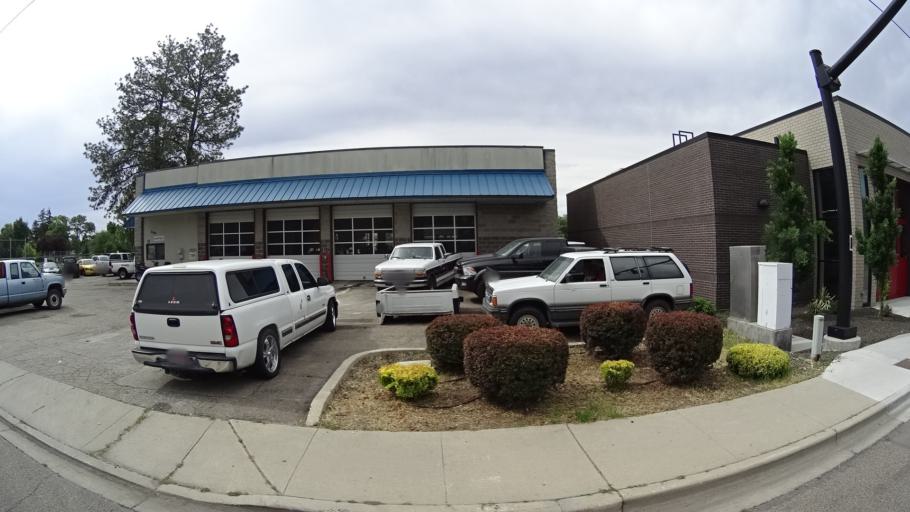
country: US
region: Idaho
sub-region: Ada County
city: Boise
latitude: 43.5896
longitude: -116.2254
